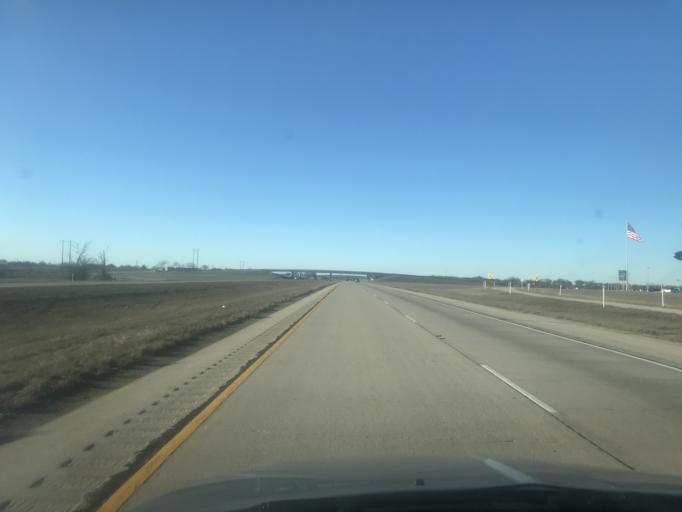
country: US
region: Texas
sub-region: Montague County
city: Bowie
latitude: 33.5132
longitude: -97.8161
